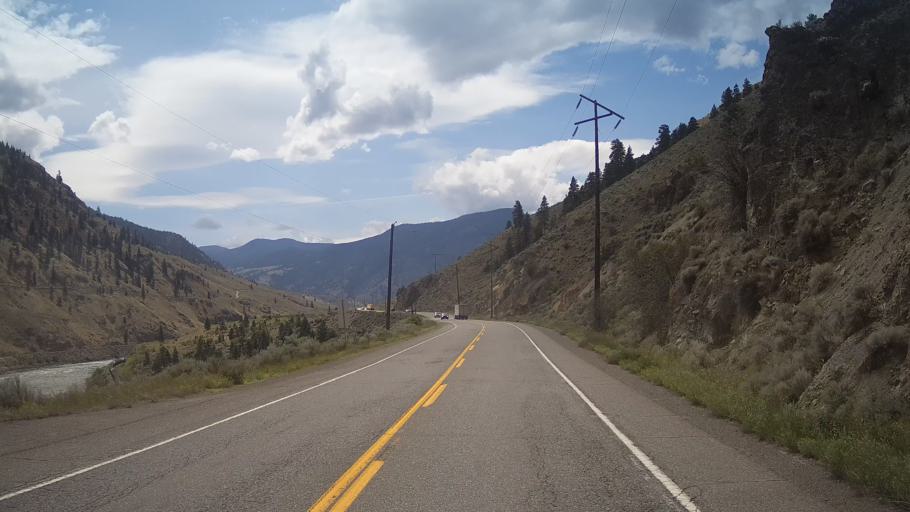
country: CA
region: British Columbia
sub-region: Thompson-Nicola Regional District
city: Ashcroft
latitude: 50.4663
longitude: -121.3005
